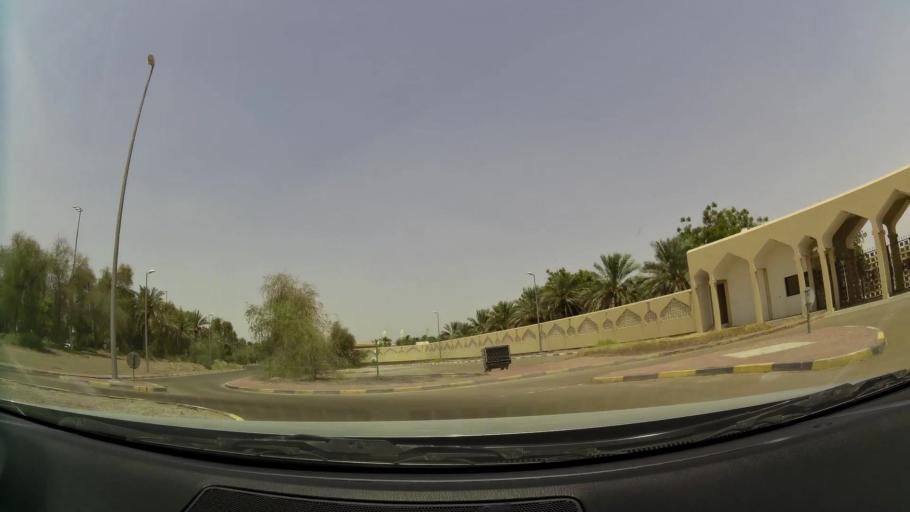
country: AE
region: Abu Dhabi
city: Al Ain
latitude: 24.2042
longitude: 55.7041
